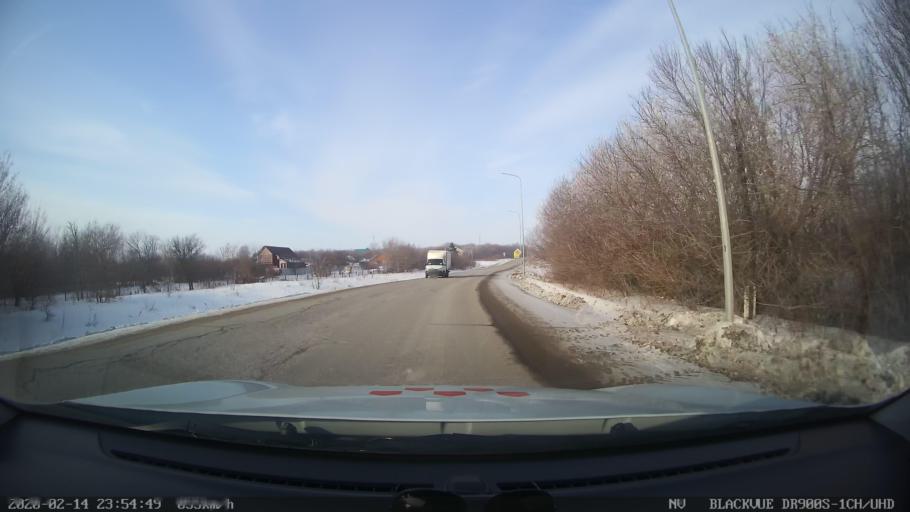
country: RU
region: Tatarstan
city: Kuybyshevskiy Zaton
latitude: 55.3119
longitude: 49.1451
